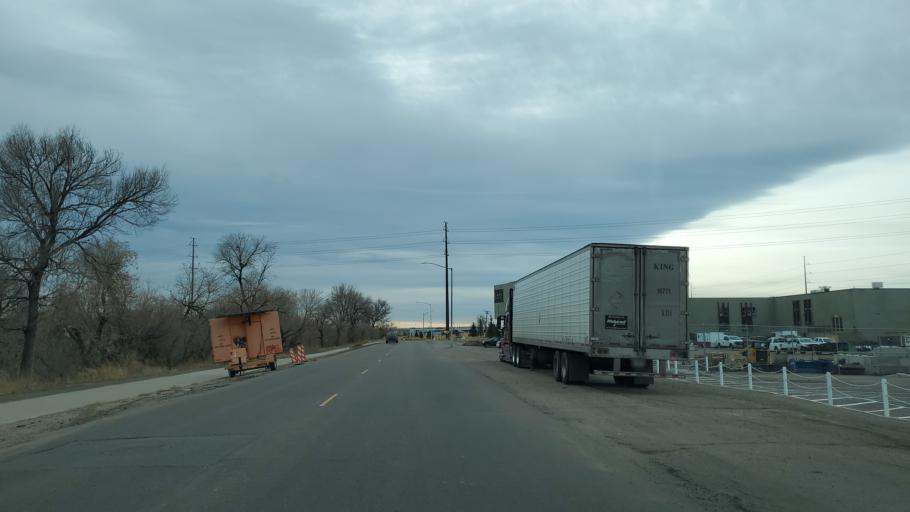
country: US
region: Colorado
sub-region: Denver County
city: Denver
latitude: 39.7097
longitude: -105.0000
